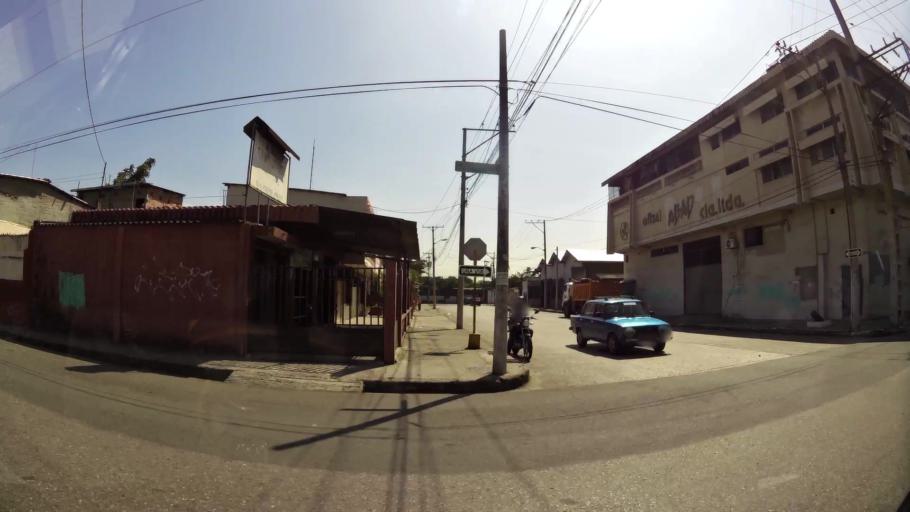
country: EC
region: Guayas
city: Guayaquil
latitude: -2.1906
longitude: -79.9003
